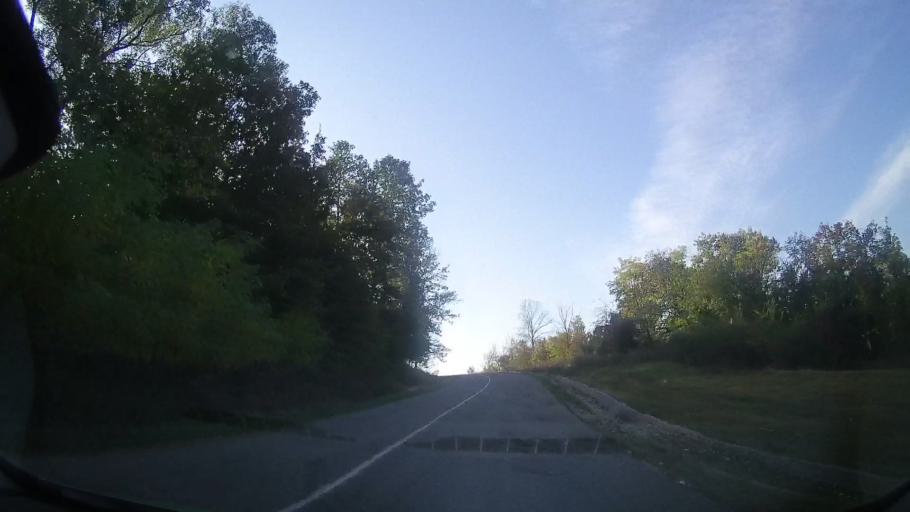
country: RO
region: Timis
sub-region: Comuna Bogda
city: Bogda
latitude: 45.9730
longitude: 21.6016
